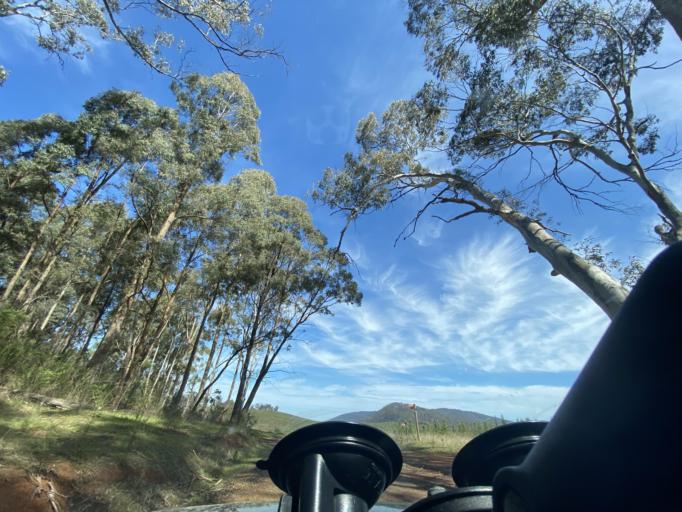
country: AU
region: Victoria
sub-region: Mansfield
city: Mansfield
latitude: -36.8169
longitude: 146.1017
